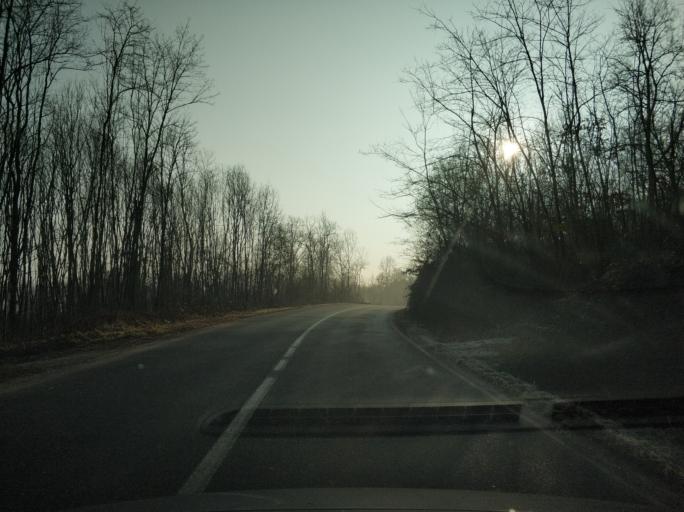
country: IT
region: Piedmont
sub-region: Provincia di Torino
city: Rivarossa
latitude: 45.2556
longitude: 7.7078
